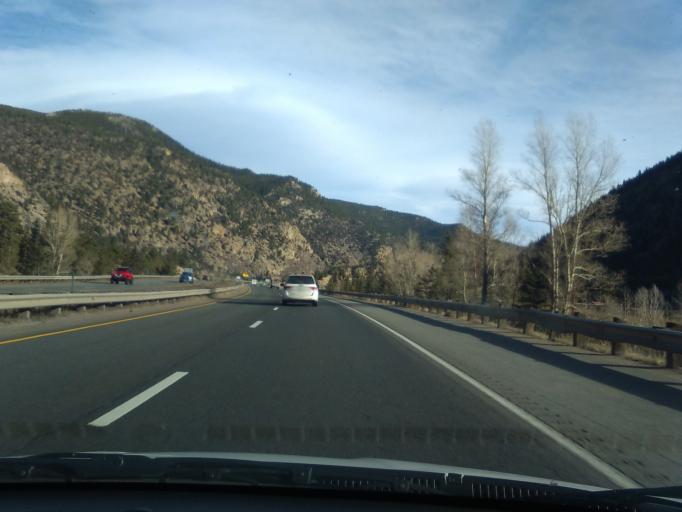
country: US
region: Colorado
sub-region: Clear Creek County
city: Georgetown
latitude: 39.7532
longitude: -105.6602
